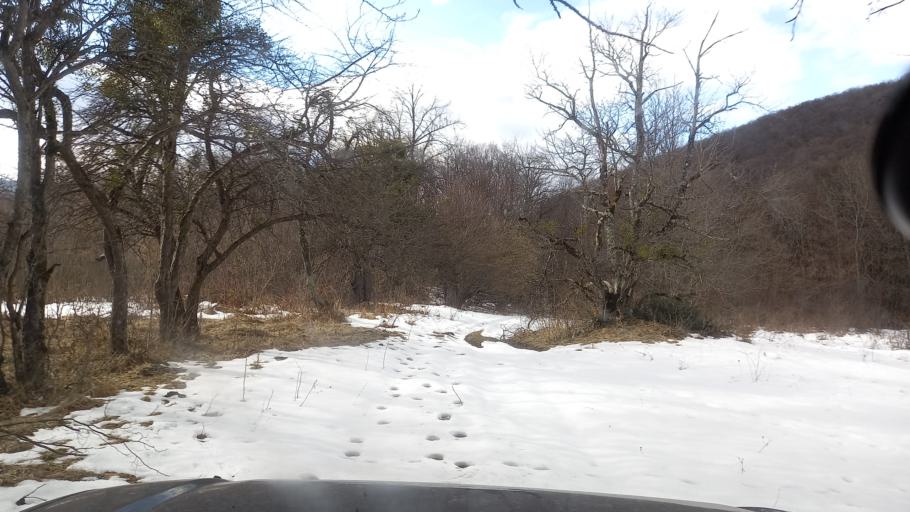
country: RU
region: Adygeya
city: Kamennomostskiy
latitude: 44.2133
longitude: 39.9653
